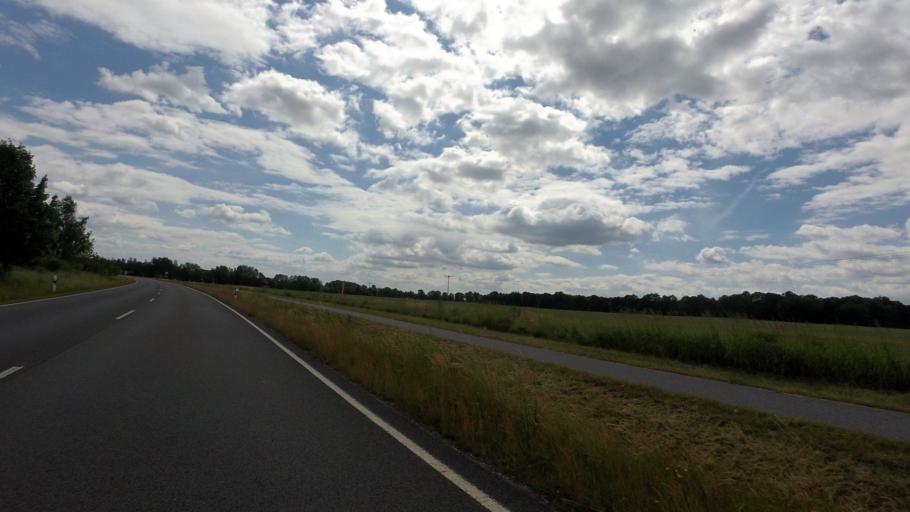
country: DE
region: Brandenburg
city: Hohenbocka
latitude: 51.4744
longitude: 14.0681
